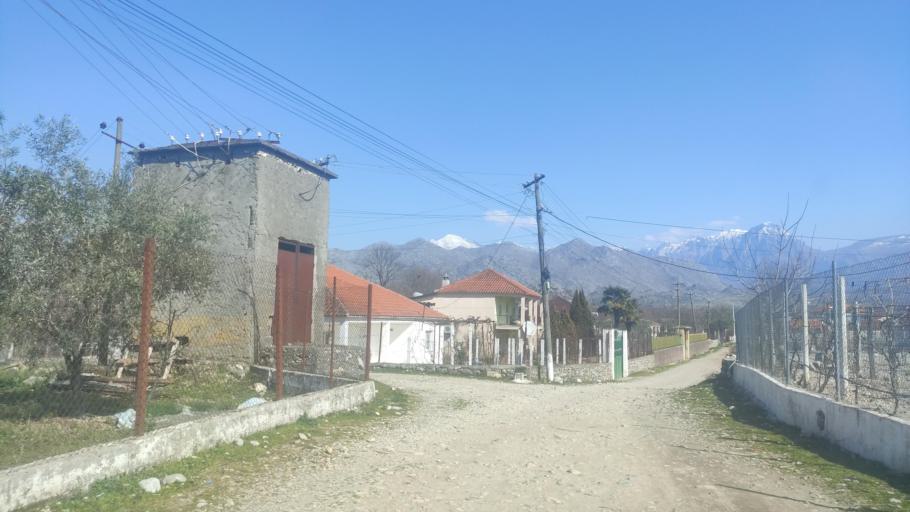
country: AL
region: Shkoder
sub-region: Rrethi i Malesia e Madhe
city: Grude-Fushe
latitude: 42.1705
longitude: 19.4827
